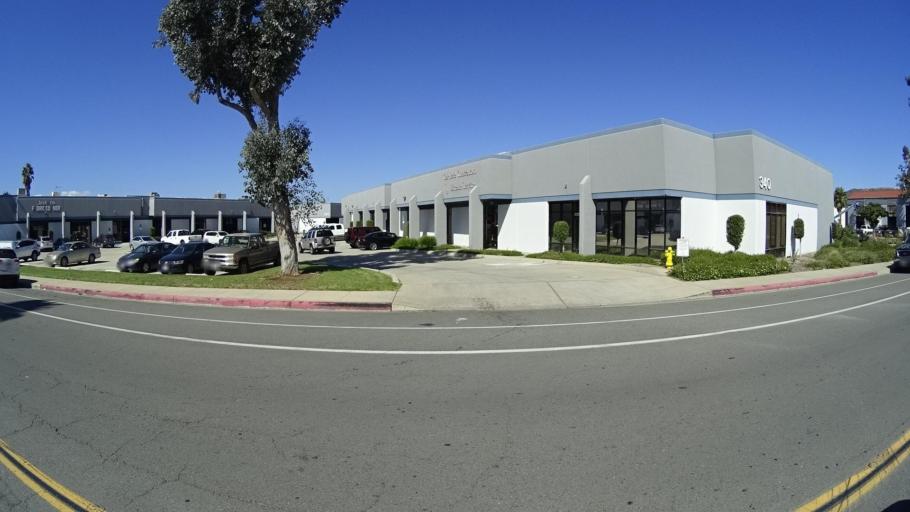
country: US
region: California
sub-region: San Diego County
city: El Cajon
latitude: 32.8127
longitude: -116.9649
